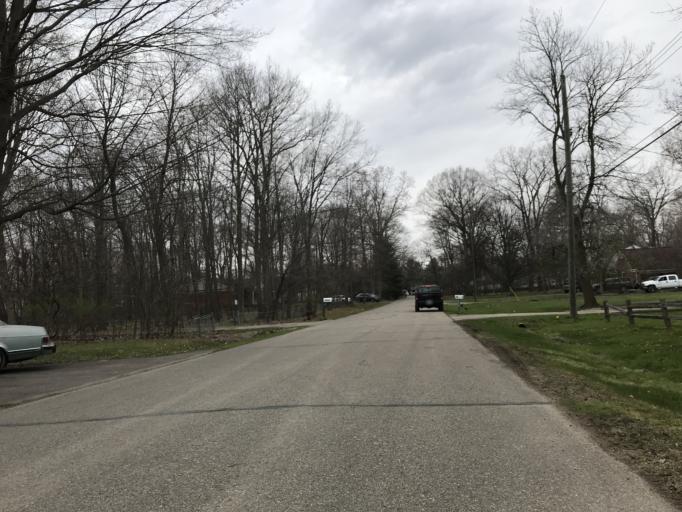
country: US
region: Michigan
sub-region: Oakland County
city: Farmington
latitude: 42.4644
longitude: -83.3402
